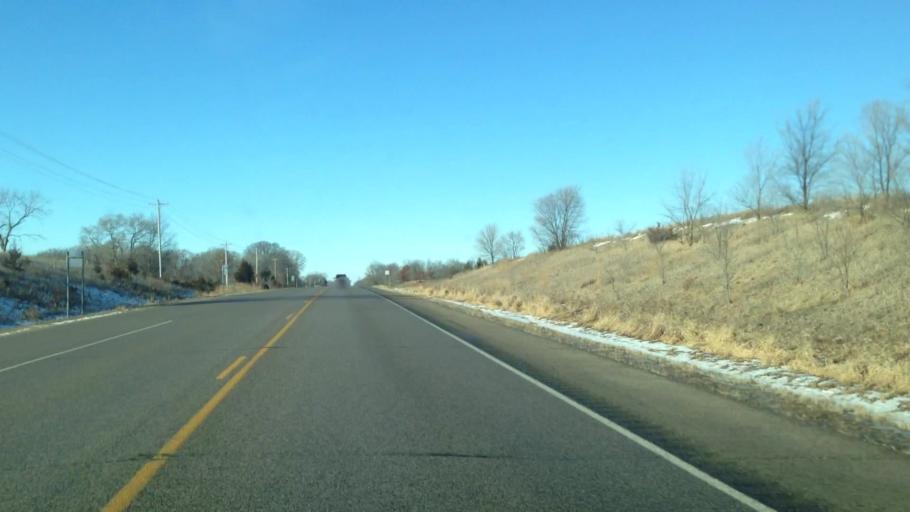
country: US
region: Minnesota
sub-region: Rice County
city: Lonsdale
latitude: 44.5437
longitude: -93.4590
